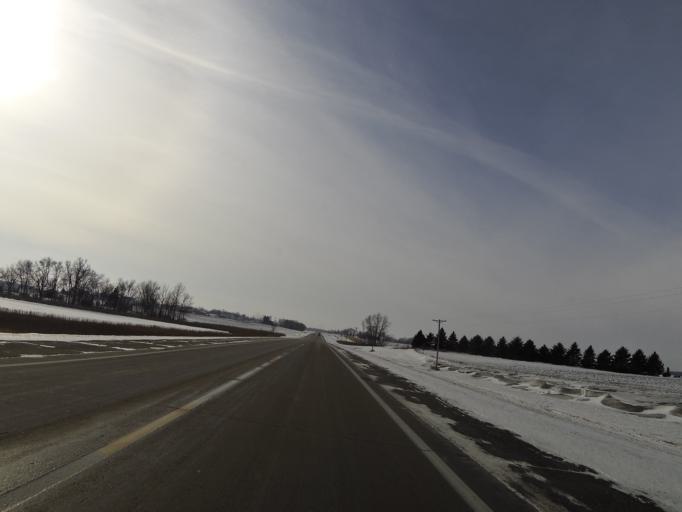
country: US
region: Minnesota
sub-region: McLeod County
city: Glencoe
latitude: 44.9007
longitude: -94.2159
